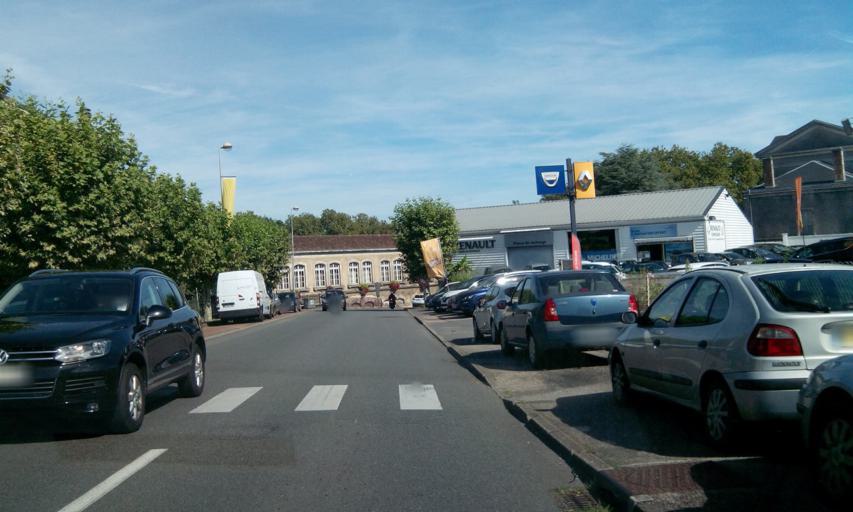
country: FR
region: Poitou-Charentes
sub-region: Departement de la Charente
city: Confolens
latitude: 46.0112
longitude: 0.6706
